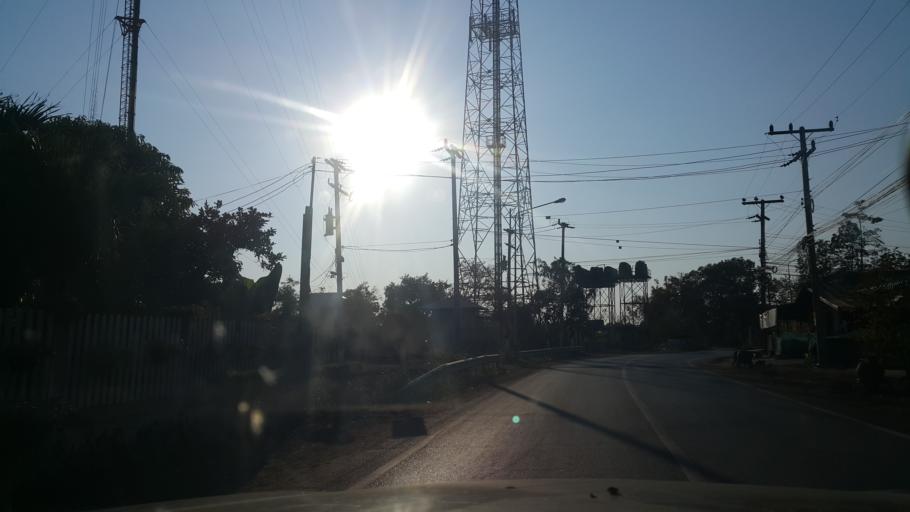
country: TH
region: Changwat Udon Thani
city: Ban Na Muang
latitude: 17.2666
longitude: 103.0023
